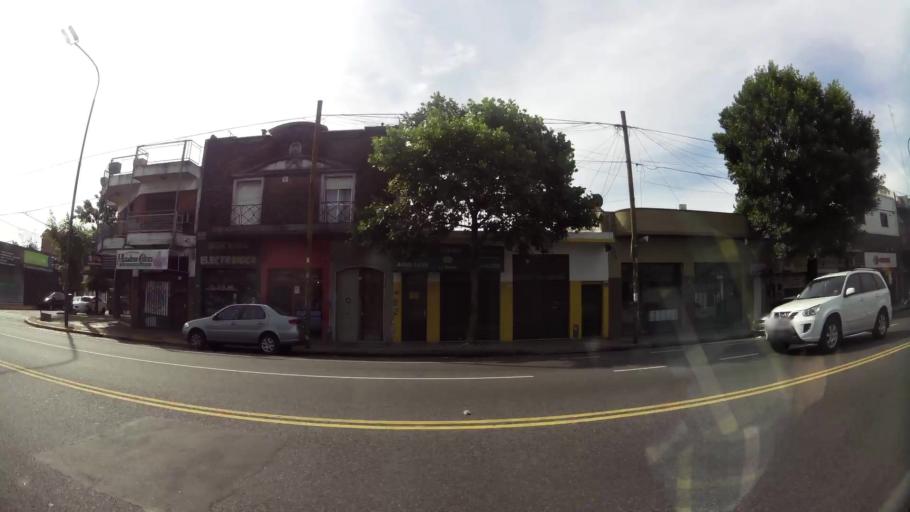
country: AR
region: Buenos Aires F.D.
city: Villa Lugano
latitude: -34.6596
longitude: -58.5132
